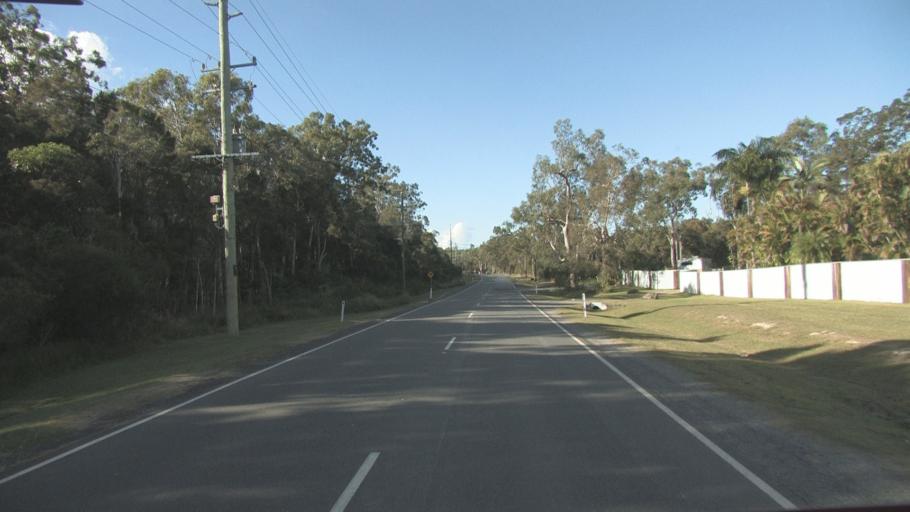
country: AU
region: Queensland
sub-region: Logan
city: Beenleigh
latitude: -27.6602
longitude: 153.2181
